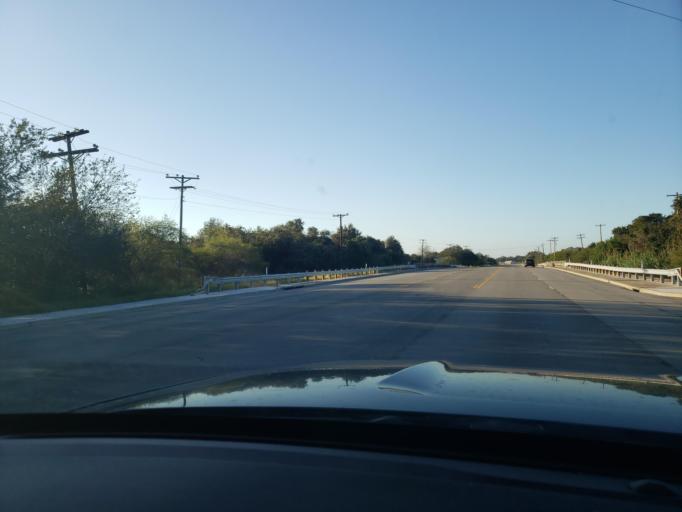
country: US
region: Texas
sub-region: Bee County
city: Beeville
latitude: 28.4281
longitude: -97.7158
